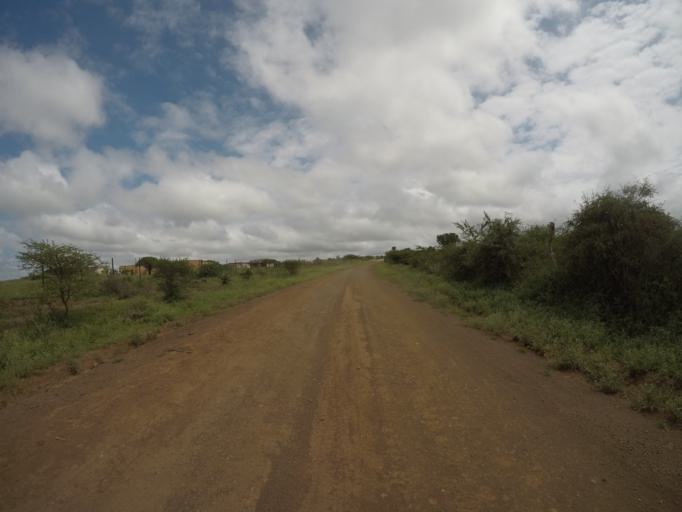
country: ZA
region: KwaZulu-Natal
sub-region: uThungulu District Municipality
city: Empangeni
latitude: -28.5825
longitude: 31.8528
